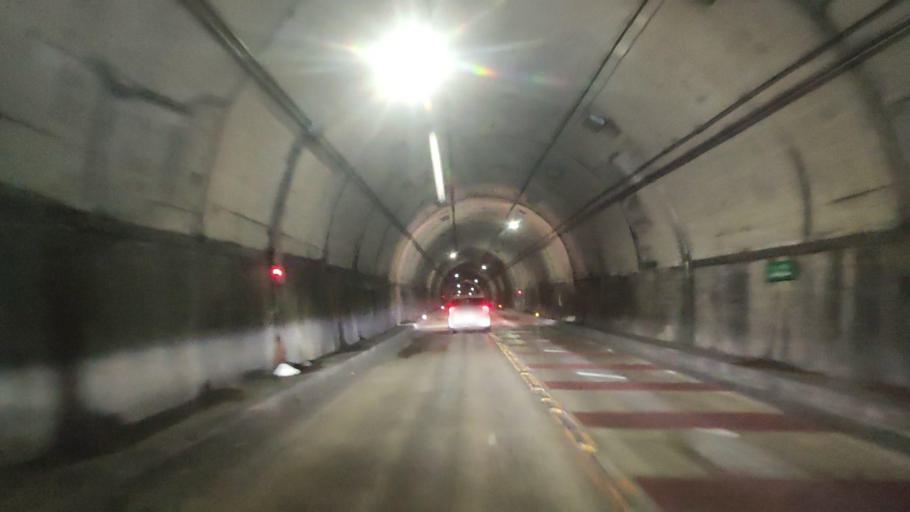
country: JP
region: Nara
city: Yoshino-cho
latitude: 34.3620
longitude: 135.9172
